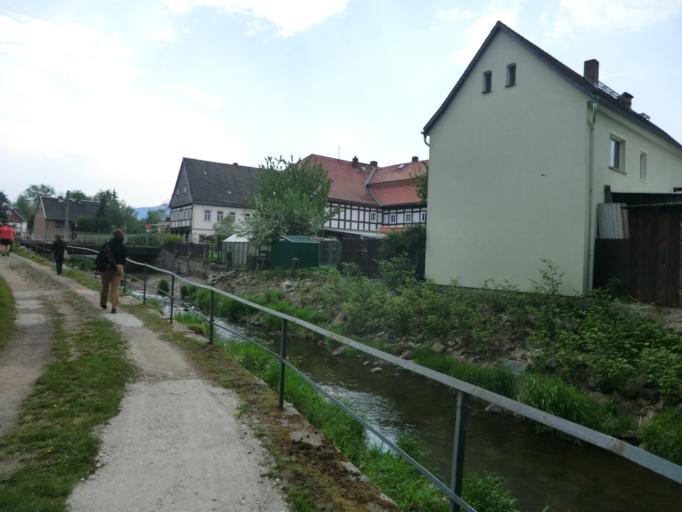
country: DE
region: Saxony
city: Grossschonau
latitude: 50.8989
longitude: 14.6656
